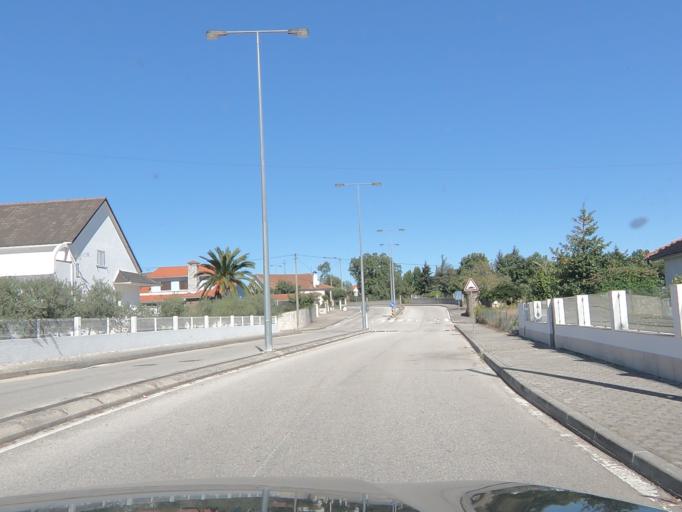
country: PT
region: Vila Real
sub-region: Valpacos
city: Valpacos
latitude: 41.6586
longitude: -7.3180
